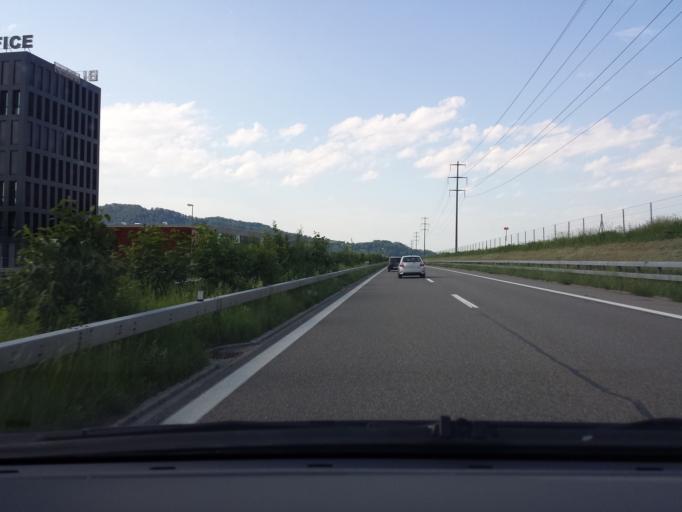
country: AT
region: Vorarlberg
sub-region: Politischer Bezirk Dornbirn
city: Lustenau
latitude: 47.4136
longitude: 9.6476
